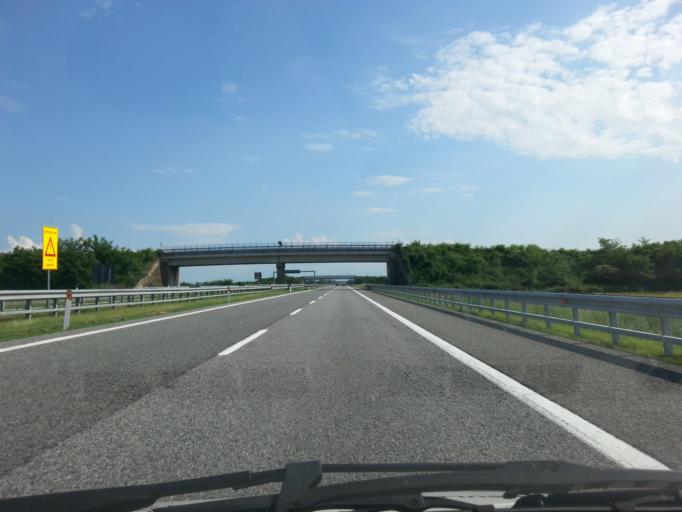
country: IT
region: Piedmont
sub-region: Provincia di Torino
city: Carmagnola
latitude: 44.8394
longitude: 7.7495
